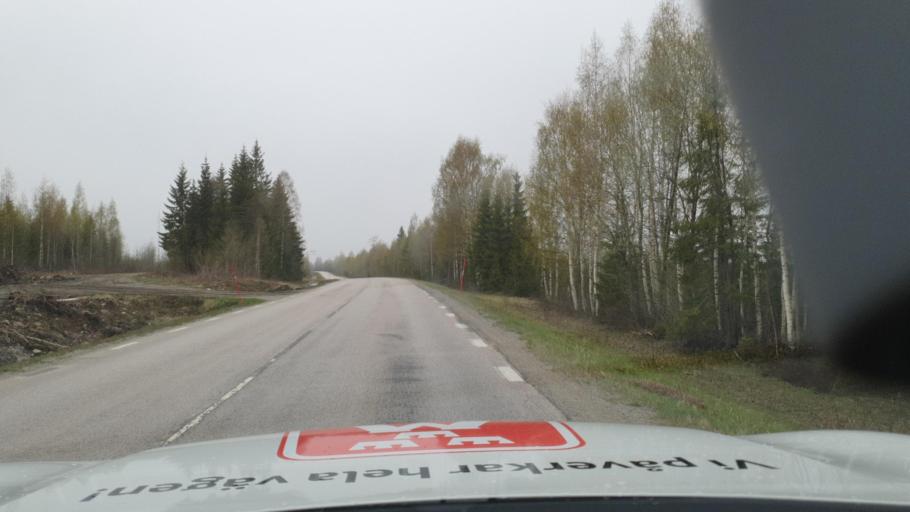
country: SE
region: Vaesterbotten
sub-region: Vannas Kommun
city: Vaennaes
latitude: 63.7919
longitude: 19.8172
